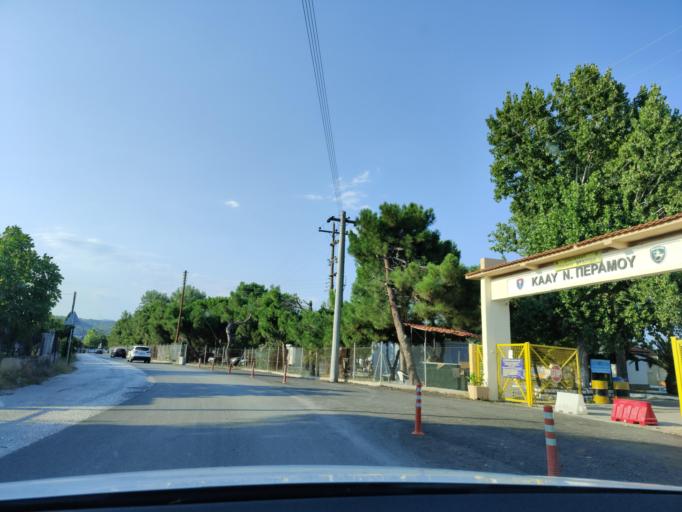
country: GR
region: East Macedonia and Thrace
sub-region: Nomos Kavalas
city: Nea Peramos
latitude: 40.8283
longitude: 24.3053
